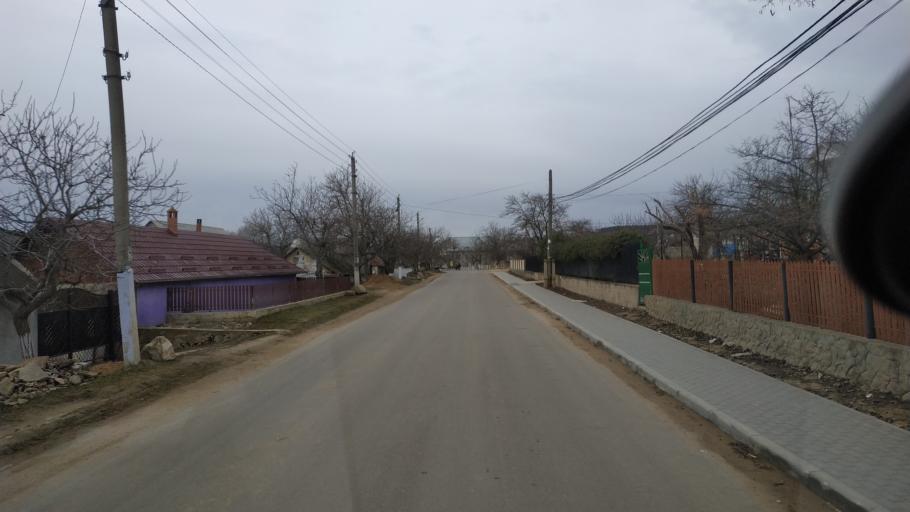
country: MD
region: Telenesti
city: Cocieri
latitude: 47.2696
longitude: 29.0610
